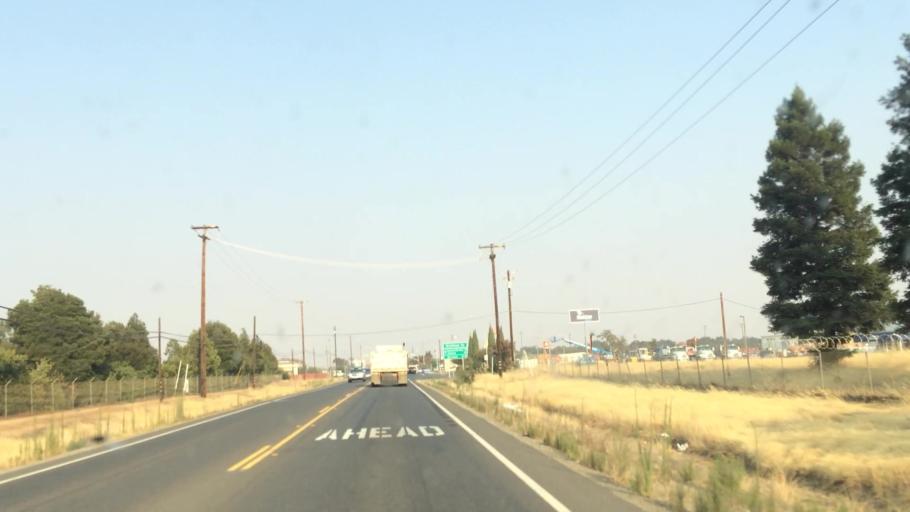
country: US
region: California
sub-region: Sacramento County
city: Rosemont
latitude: 38.5299
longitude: -121.3384
